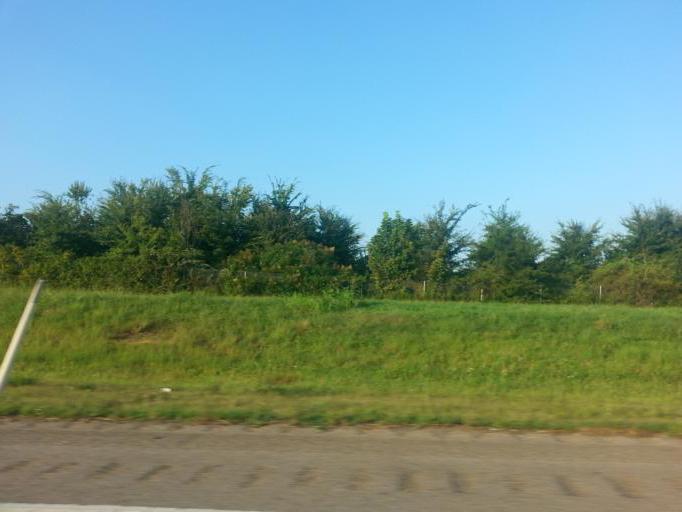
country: US
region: Tennessee
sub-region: Blount County
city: Eagleton Village
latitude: 35.8086
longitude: -83.9433
